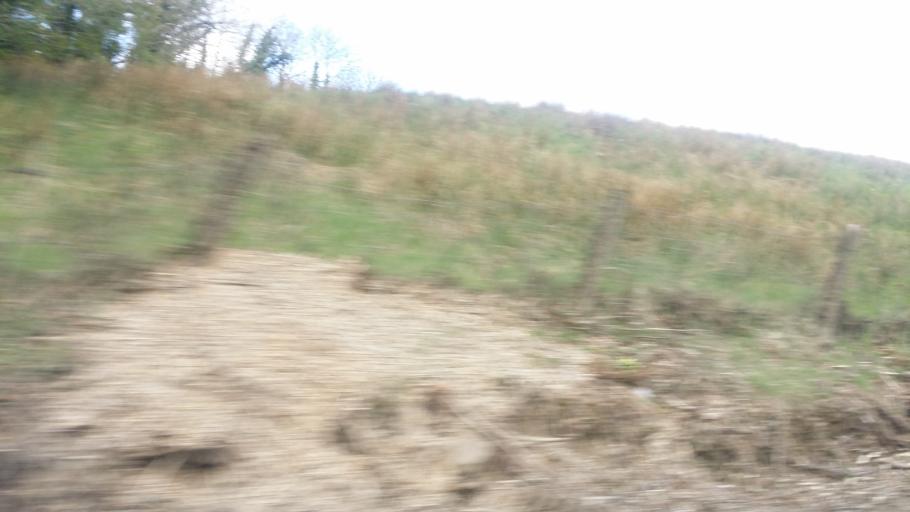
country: IE
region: Ulster
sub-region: An Cabhan
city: Ballyjamesduff
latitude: 53.9448
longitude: -7.2257
